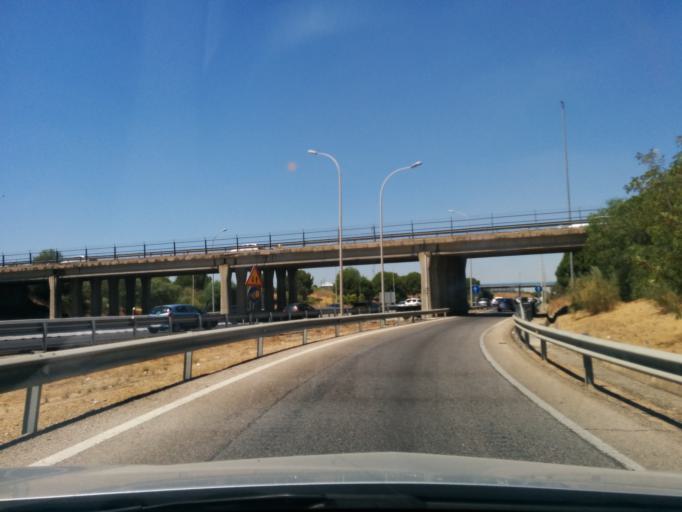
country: ES
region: Andalusia
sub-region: Provincia de Sevilla
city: Benacazon
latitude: 37.3614
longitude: -6.1995
